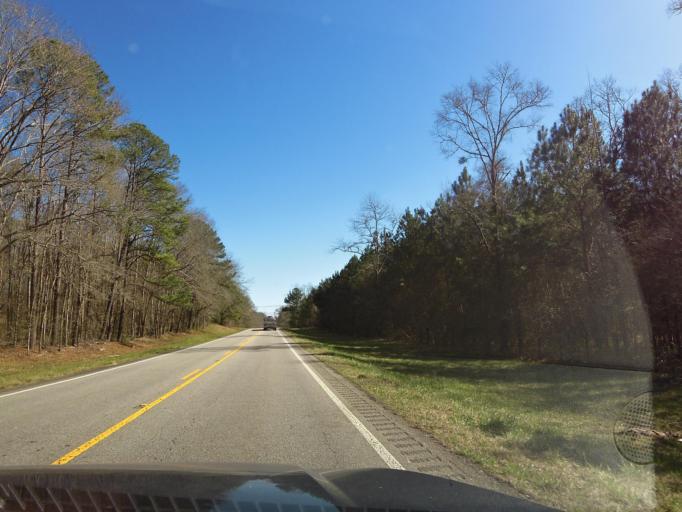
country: US
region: Alabama
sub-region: Bullock County
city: Union Springs
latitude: 32.0854
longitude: -85.5415
